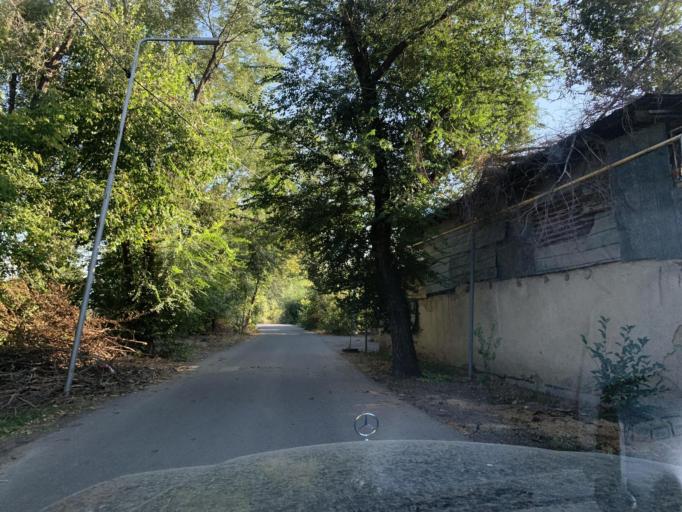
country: KZ
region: Almaty Oblysy
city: Energeticheskiy
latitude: 43.3906
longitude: 76.9996
